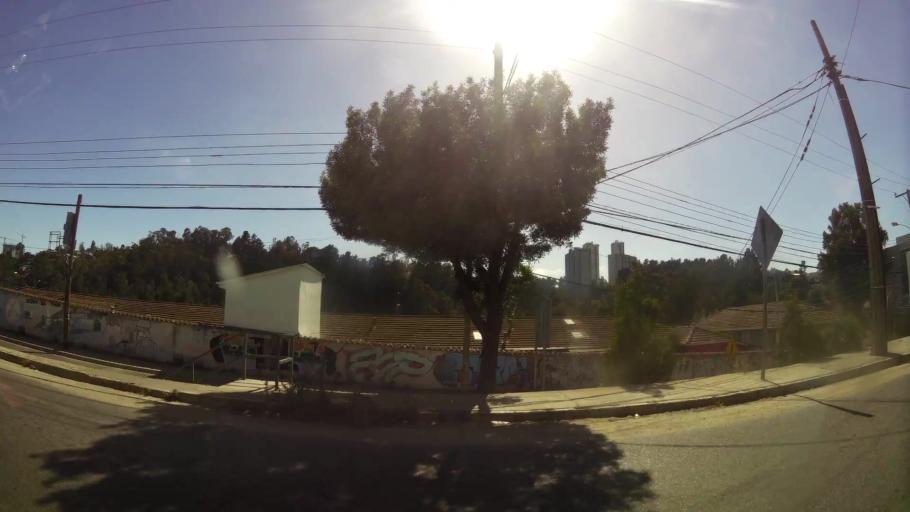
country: CL
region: Valparaiso
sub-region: Provincia de Valparaiso
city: Valparaiso
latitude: -33.0600
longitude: -71.5932
